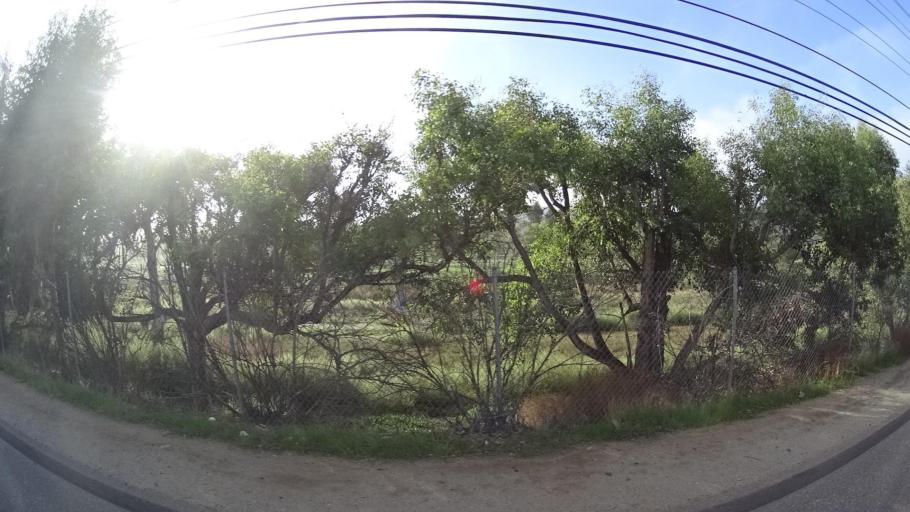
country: US
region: California
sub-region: San Diego County
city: Rancho San Diego
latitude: 32.7438
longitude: -116.9195
